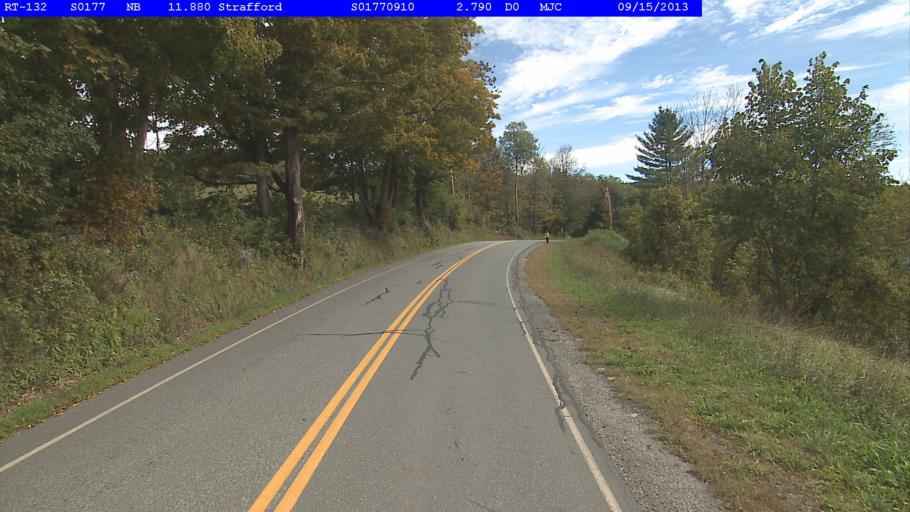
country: US
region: New Hampshire
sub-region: Grafton County
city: Hanover
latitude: 43.8375
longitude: -72.3557
